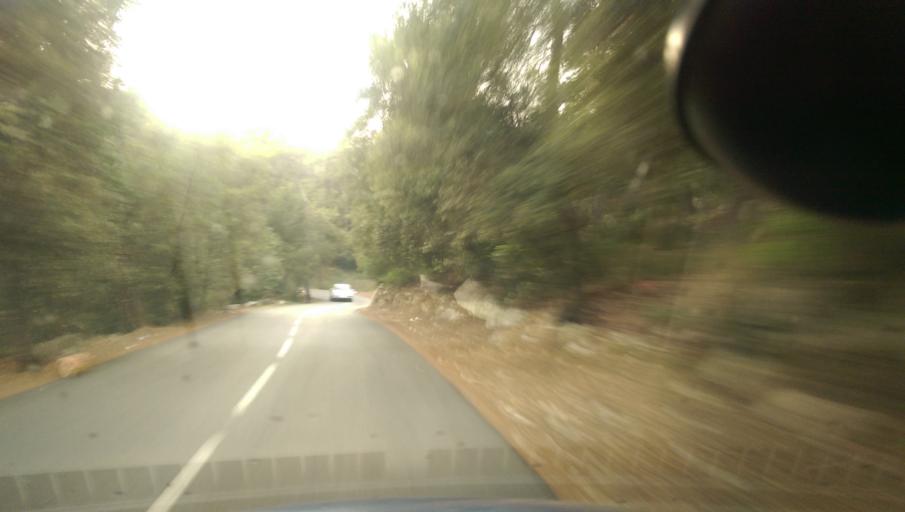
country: FR
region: Provence-Alpes-Cote d'Azur
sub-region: Departement des Alpes-Maritimes
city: Valbonne
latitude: 43.6395
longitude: 7.0414
